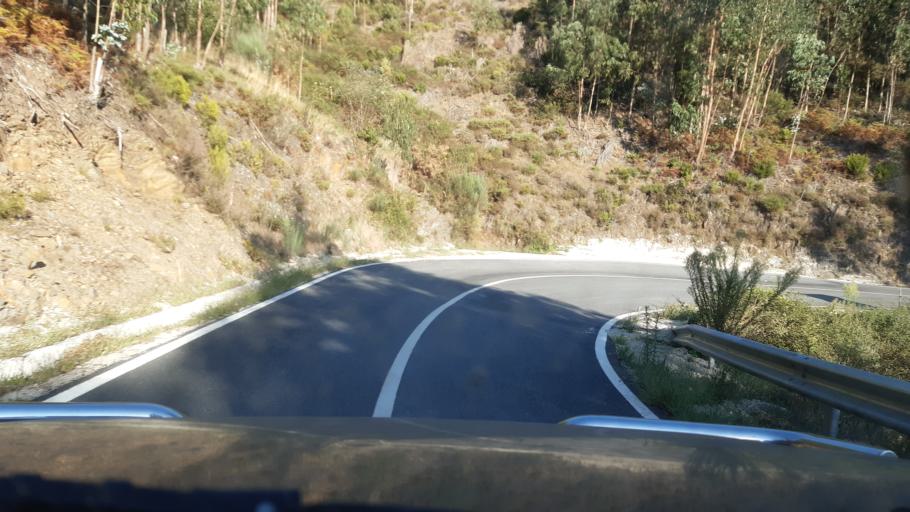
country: PT
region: Viseu
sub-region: Mortagua
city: Mortagua
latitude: 40.5376
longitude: -8.2452
